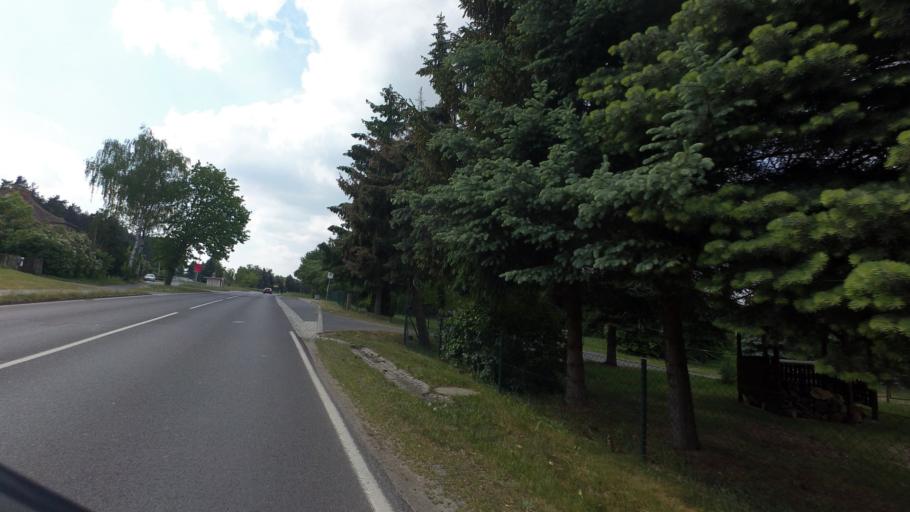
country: DE
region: Saxony
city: Quitzdorf
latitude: 51.2932
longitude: 14.7852
